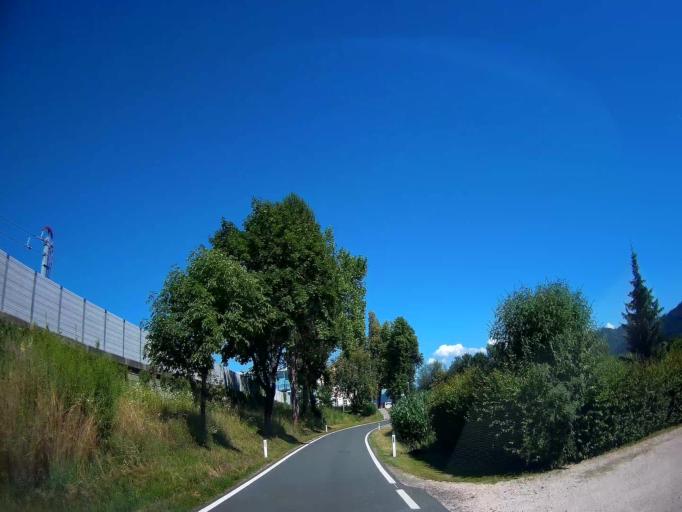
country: AT
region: Carinthia
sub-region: Politischer Bezirk Klagenfurt Land
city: Grafenstein
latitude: 46.6191
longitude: 14.4579
